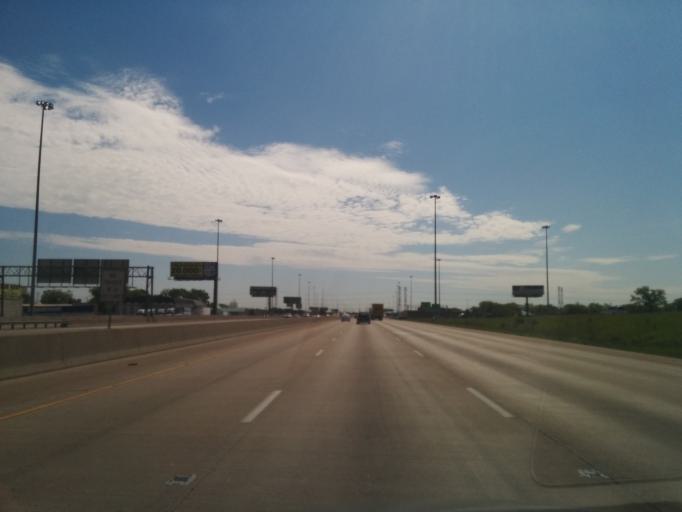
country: US
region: Illinois
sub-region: Cook County
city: Lansing
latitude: 41.5777
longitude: -87.5722
